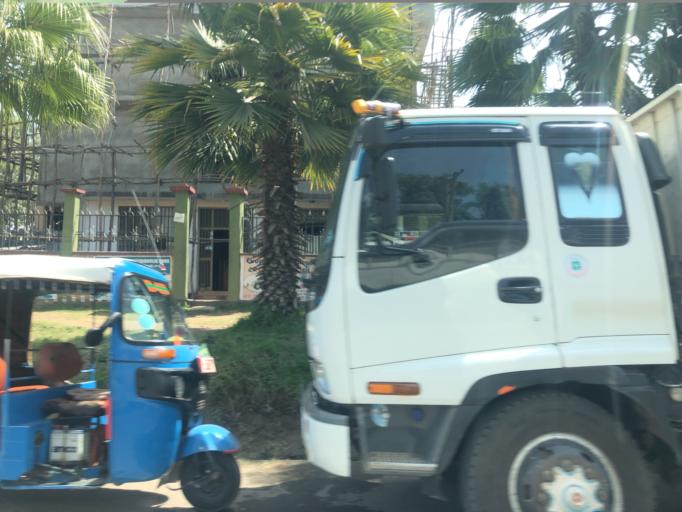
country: ET
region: Oromiya
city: Shashemene
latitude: 7.2021
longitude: 38.6076
